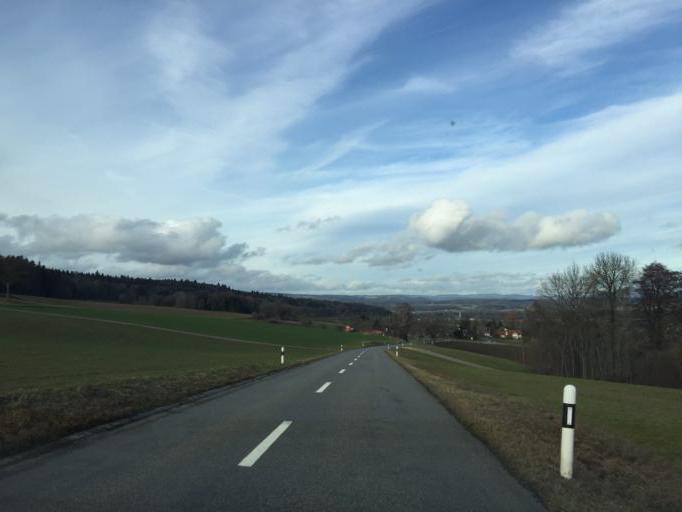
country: DE
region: Baden-Wuerttemberg
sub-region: Freiburg Region
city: Busingen
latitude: 47.6533
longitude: 8.6905
